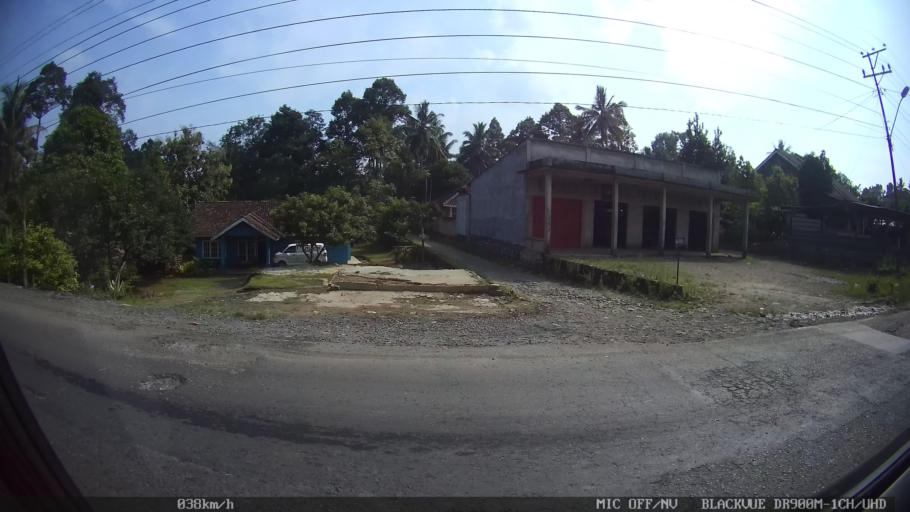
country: ID
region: Lampung
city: Natar
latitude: -5.3688
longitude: 105.1722
